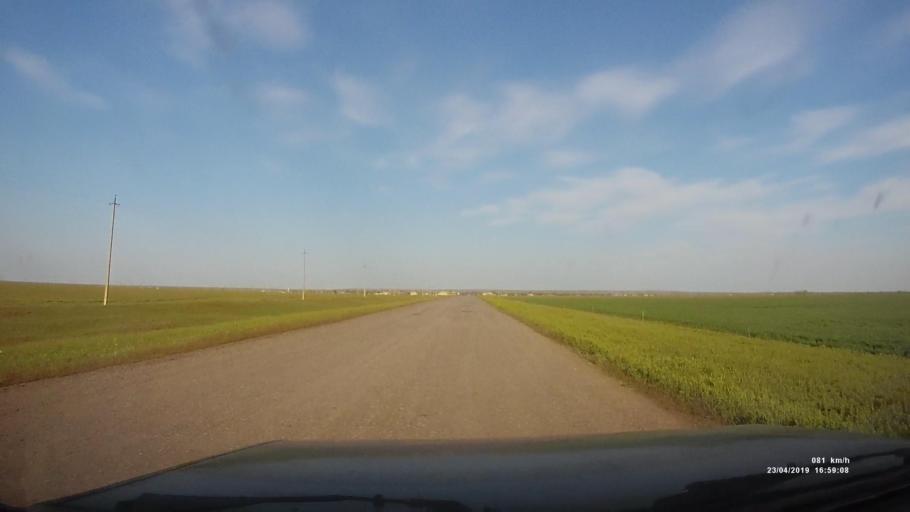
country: RU
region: Kalmykiya
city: Priyutnoye
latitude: 46.3082
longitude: 43.3846
